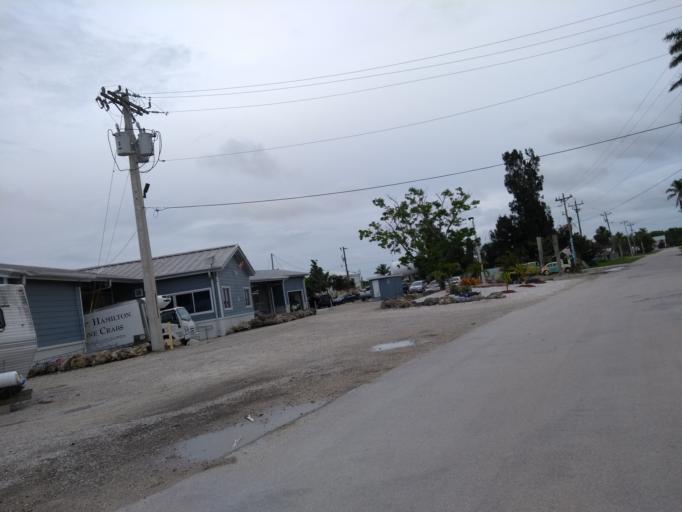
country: US
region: Florida
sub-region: Collier County
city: Marco
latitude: 25.8656
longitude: -81.3865
